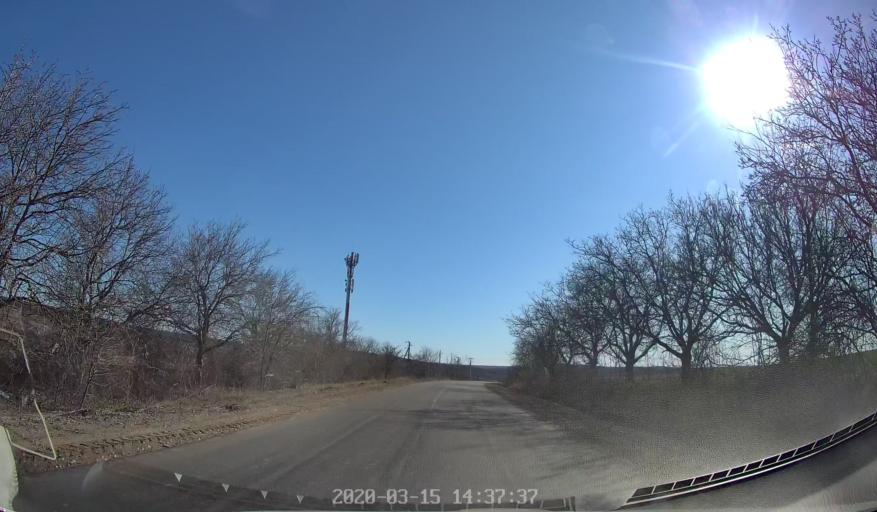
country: MD
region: Orhei
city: Orhei
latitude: 47.3135
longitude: 28.9247
